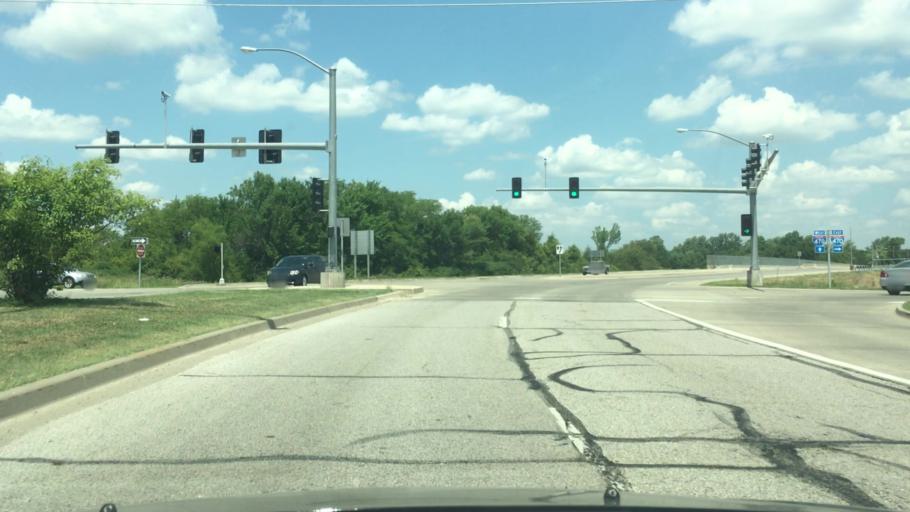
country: US
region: Missouri
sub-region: Jackson County
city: Lees Summit
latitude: 38.9337
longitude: -94.4024
